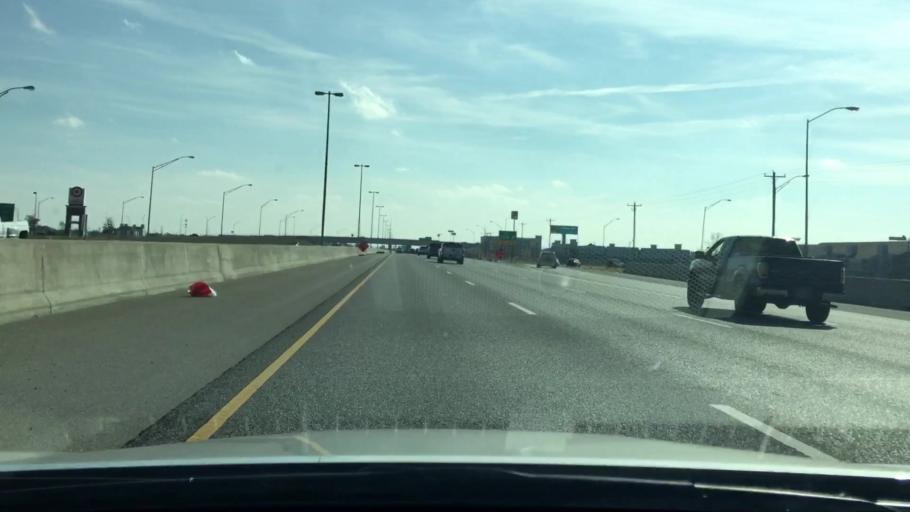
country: US
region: Oklahoma
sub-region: Cleveland County
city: Norman
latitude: 35.2378
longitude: -97.4856
